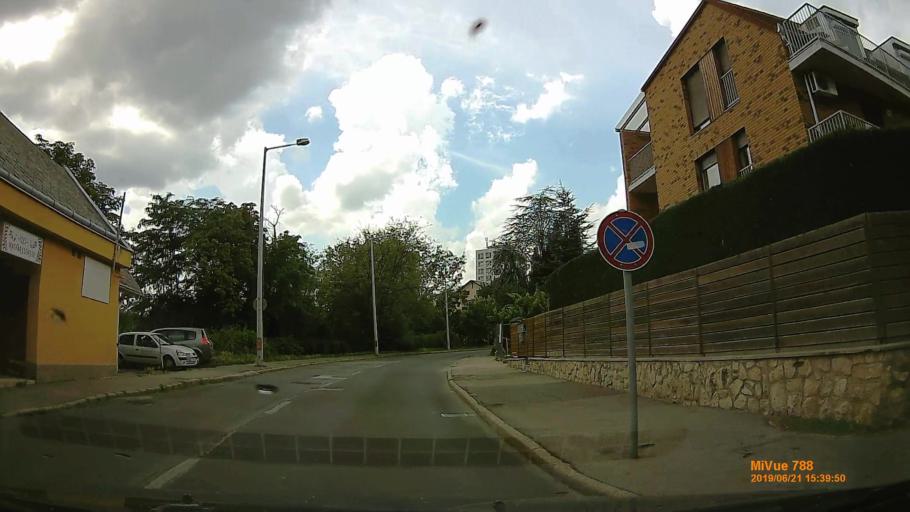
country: HU
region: Baranya
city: Pecs
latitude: 46.0807
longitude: 18.2165
